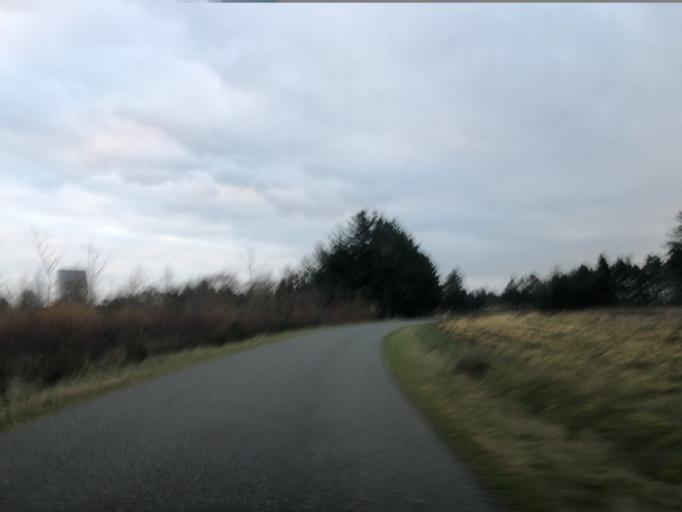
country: DK
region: Central Jutland
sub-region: Holstebro Kommune
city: Ulfborg
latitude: 56.2448
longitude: 8.2874
